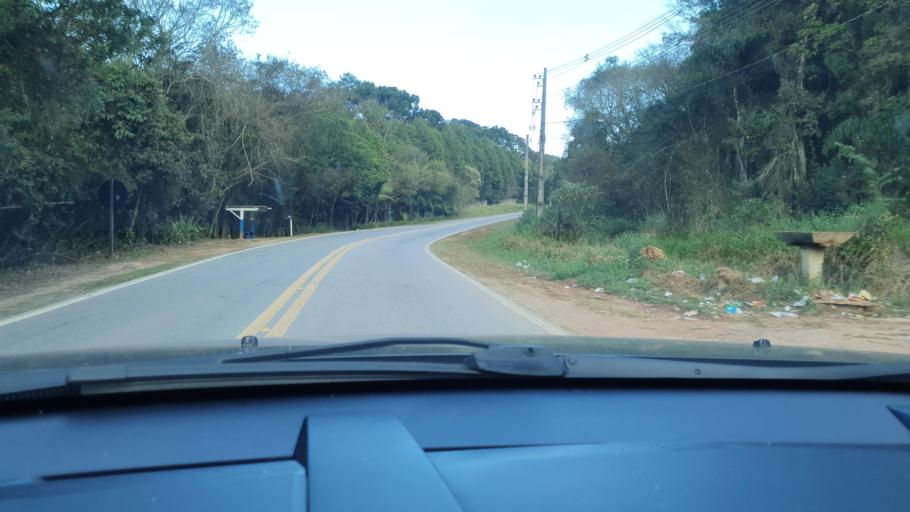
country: BR
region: Sao Paulo
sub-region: Ibiuna
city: Ibiuna
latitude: -23.6766
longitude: -47.2931
